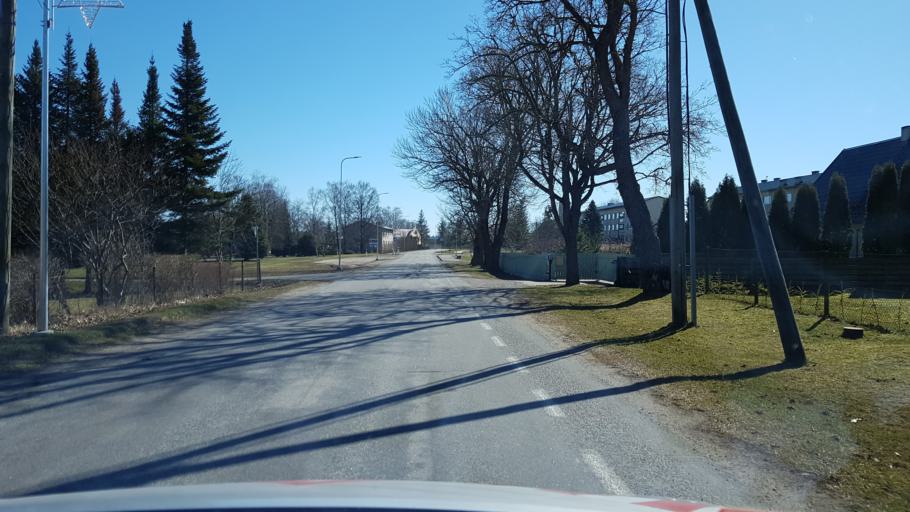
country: EE
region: Laeaene-Virumaa
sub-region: Haljala vald
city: Haljala
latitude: 59.4336
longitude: 26.2595
